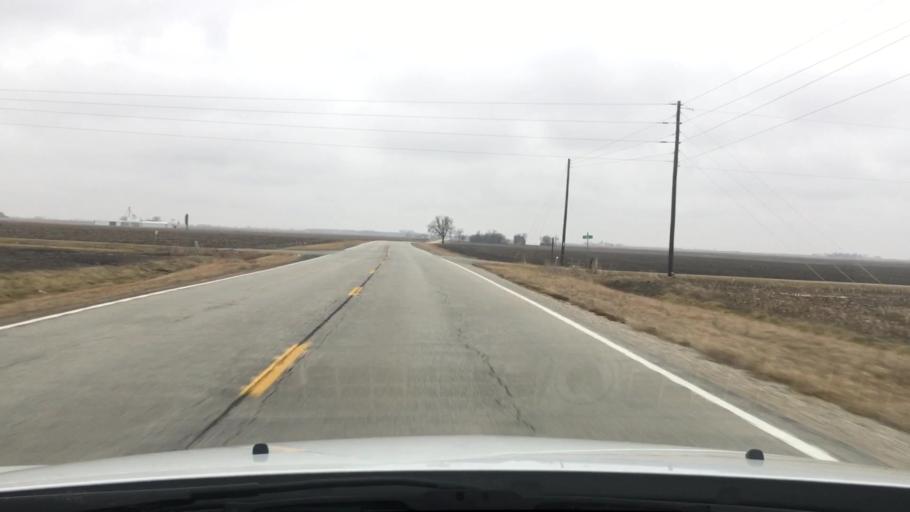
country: US
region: Illinois
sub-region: Iroquois County
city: Clifton
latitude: 40.8869
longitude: -87.8840
